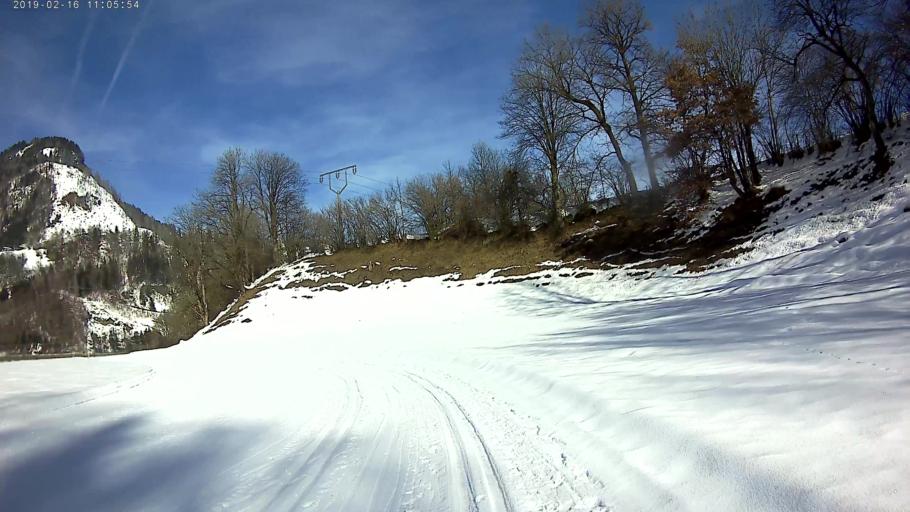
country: AT
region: Salzburg
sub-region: Politischer Bezirk Sankt Johann im Pongau
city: Sankt Johann im Pongau
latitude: 47.3255
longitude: 13.1881
